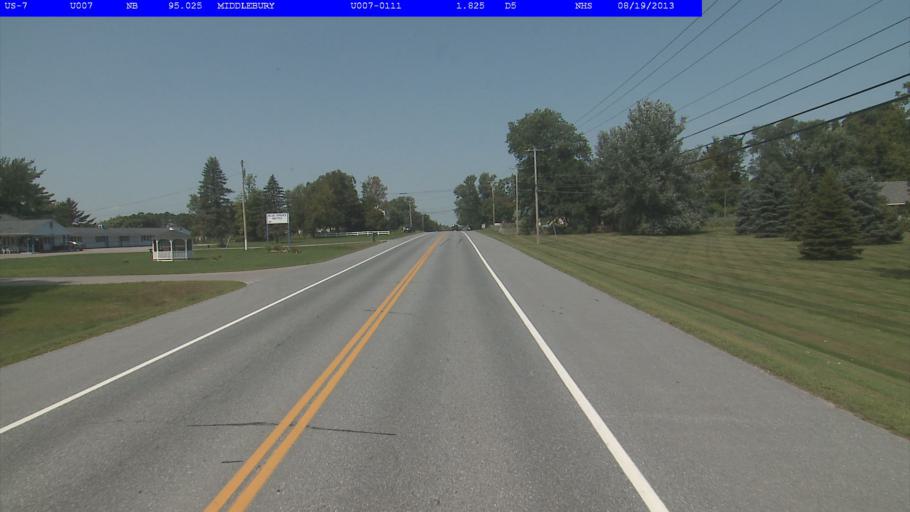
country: US
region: Vermont
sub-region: Addison County
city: Middlebury (village)
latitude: 43.9803
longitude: -73.1239
